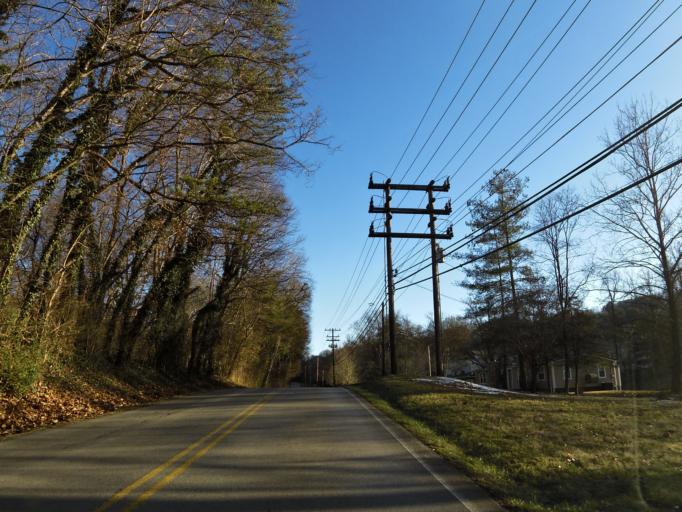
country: US
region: Tennessee
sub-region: Knox County
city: Farragut
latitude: 35.8909
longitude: -84.1348
